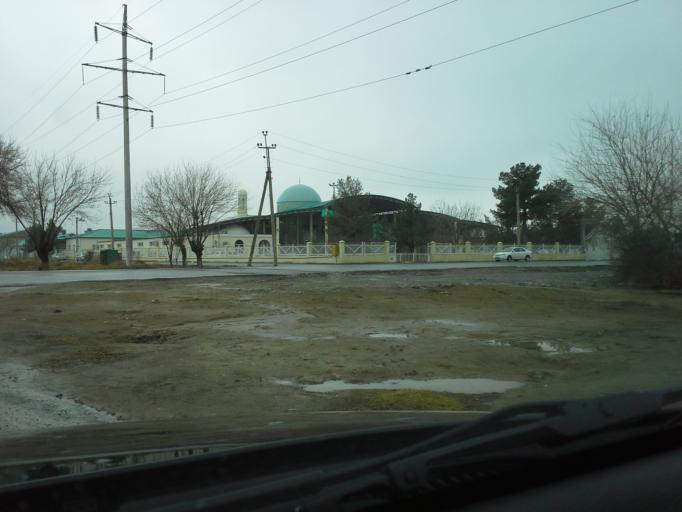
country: TM
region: Ahal
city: Ashgabat
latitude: 37.9520
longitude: 58.4199
